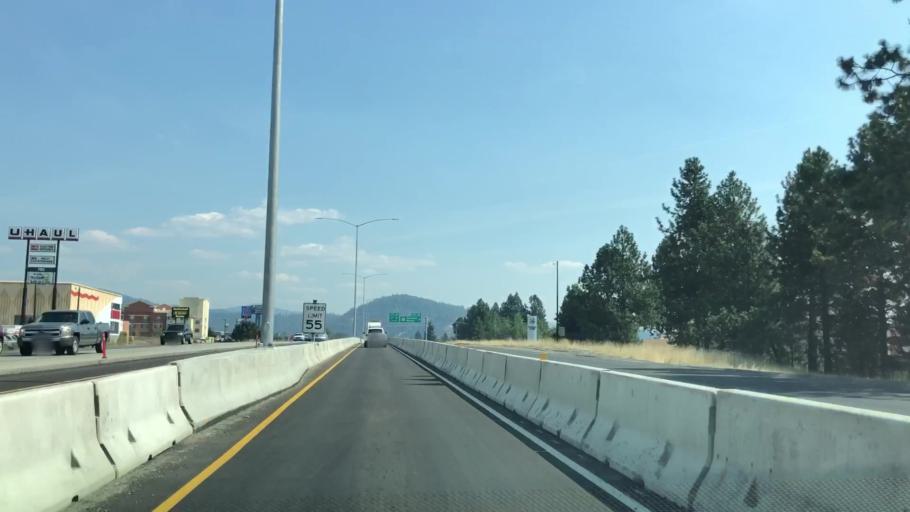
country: US
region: Idaho
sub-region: Kootenai County
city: Coeur d'Alene
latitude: 47.6991
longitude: -116.8008
